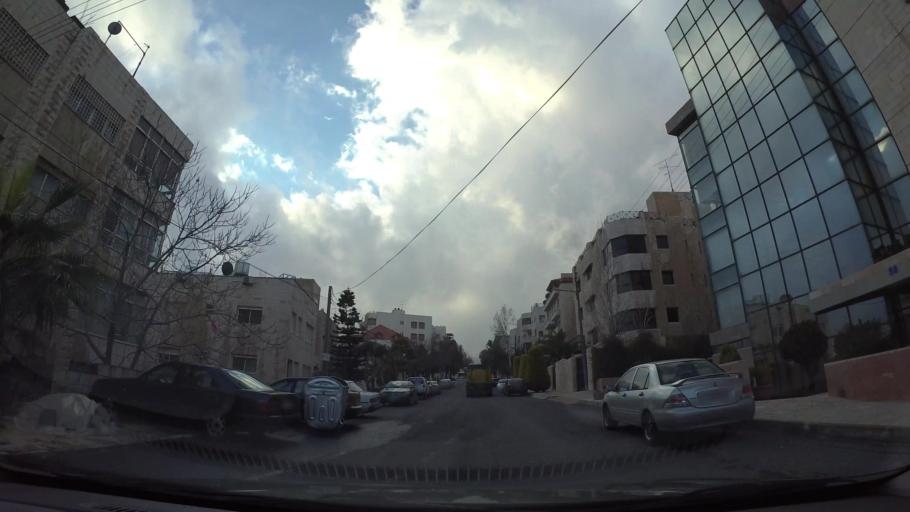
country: JO
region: Amman
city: Amman
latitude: 31.9551
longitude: 35.8877
